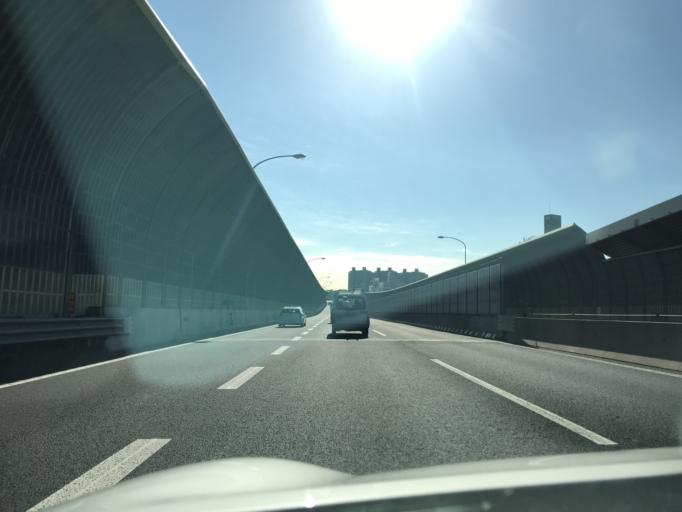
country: JP
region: Chiba
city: Chiba
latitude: 35.6349
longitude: 140.1226
